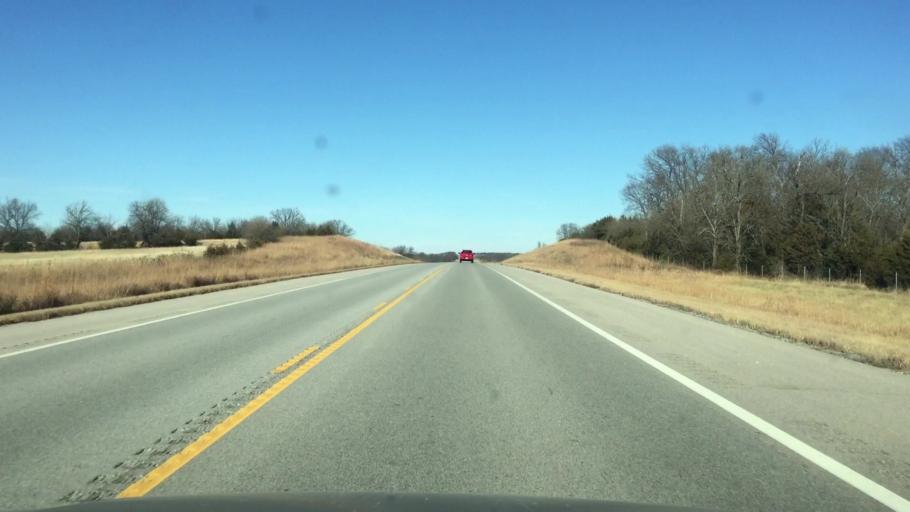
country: US
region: Kansas
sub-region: Allen County
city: Iola
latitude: 37.9701
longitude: -95.3811
